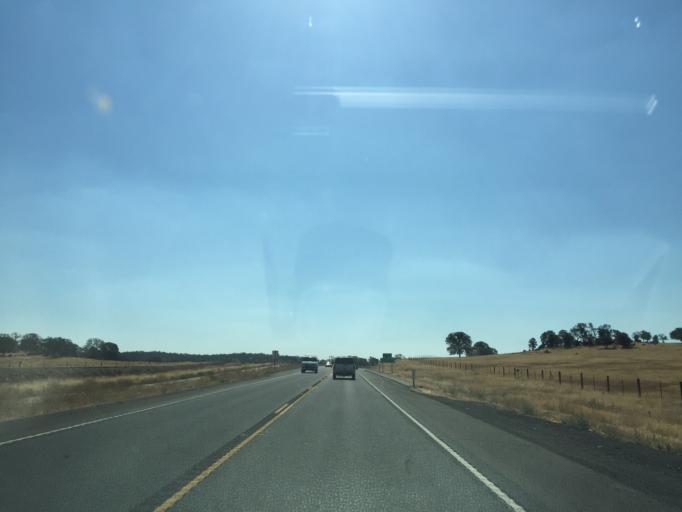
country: US
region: California
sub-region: Tuolumne County
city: Jamestown
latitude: 37.8487
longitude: -120.5077
